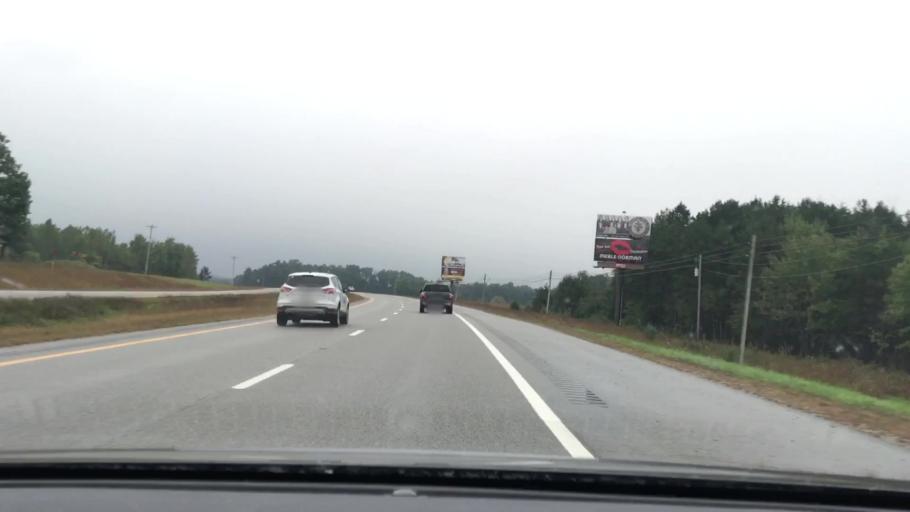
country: US
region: Tennessee
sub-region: Fentress County
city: Grimsley
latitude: 36.3393
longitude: -84.9533
